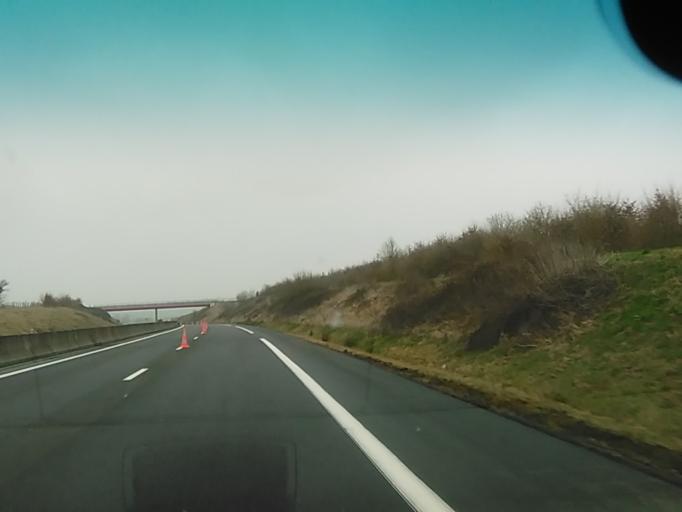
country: FR
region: Lower Normandy
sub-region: Departement de l'Orne
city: Gace
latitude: 48.7094
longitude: 0.2520
